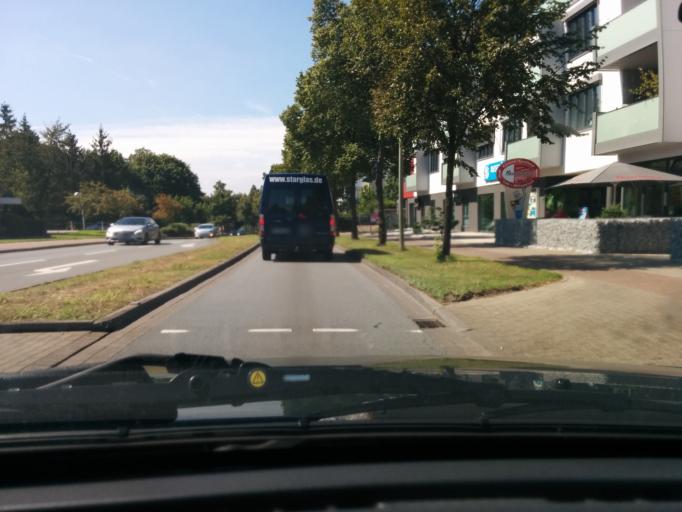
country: DE
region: North Rhine-Westphalia
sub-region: Regierungsbezirk Detmold
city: Bielefeld
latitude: 52.0582
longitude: 8.5438
